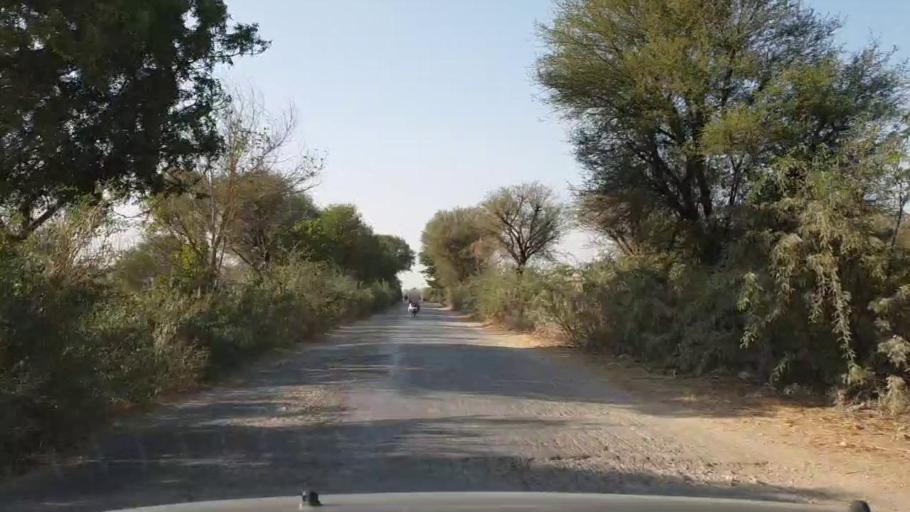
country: PK
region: Sindh
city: Tando Ghulam Ali
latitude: 25.1491
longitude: 68.8619
